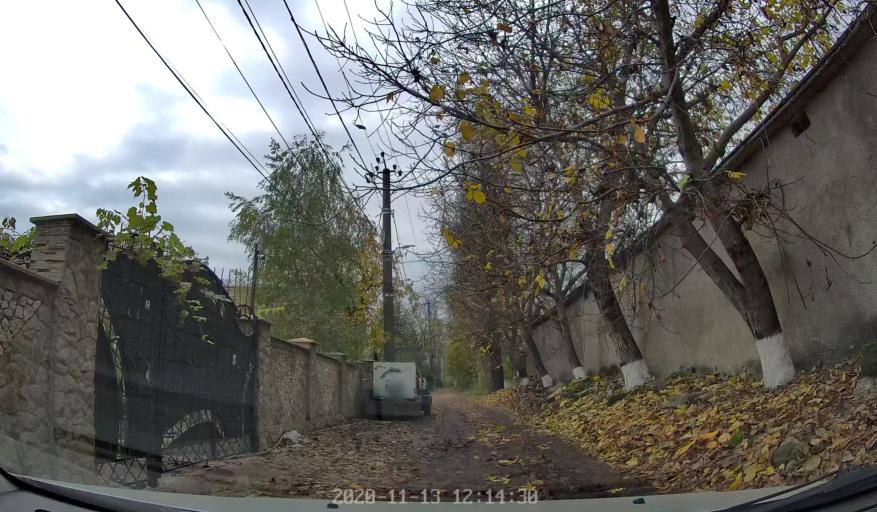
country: MD
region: Chisinau
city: Chisinau
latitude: 46.9527
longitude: 28.8380
